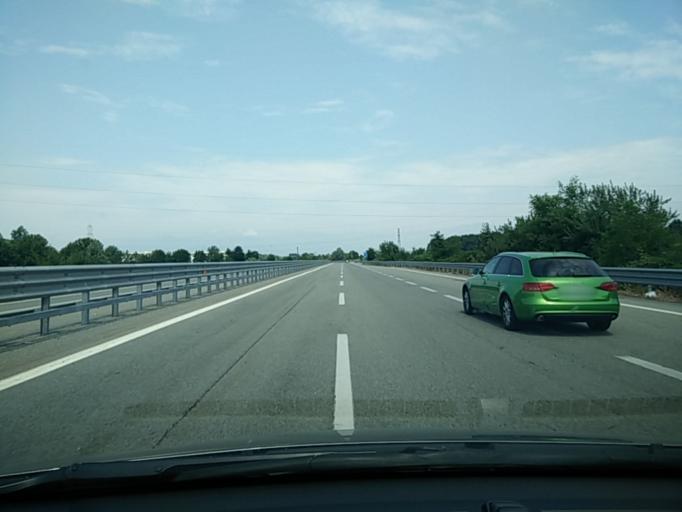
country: IT
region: Piedmont
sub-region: Provincia di Torino
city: Brandizzo
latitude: 45.1744
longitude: 7.8054
